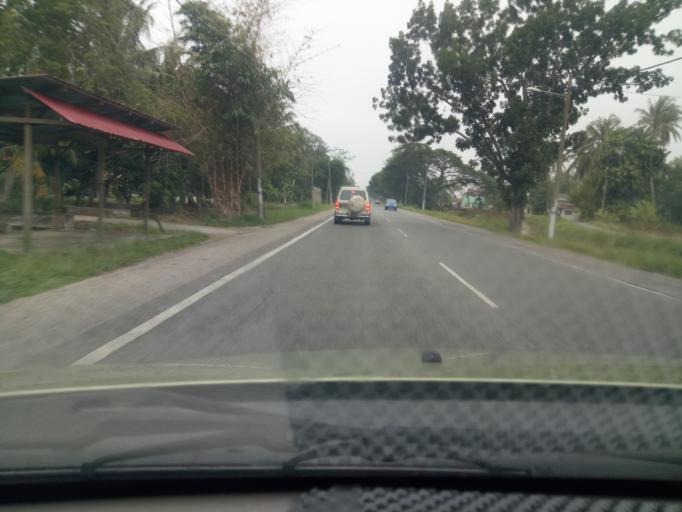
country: MY
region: Kedah
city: Gurun
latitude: 5.9042
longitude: 100.4334
